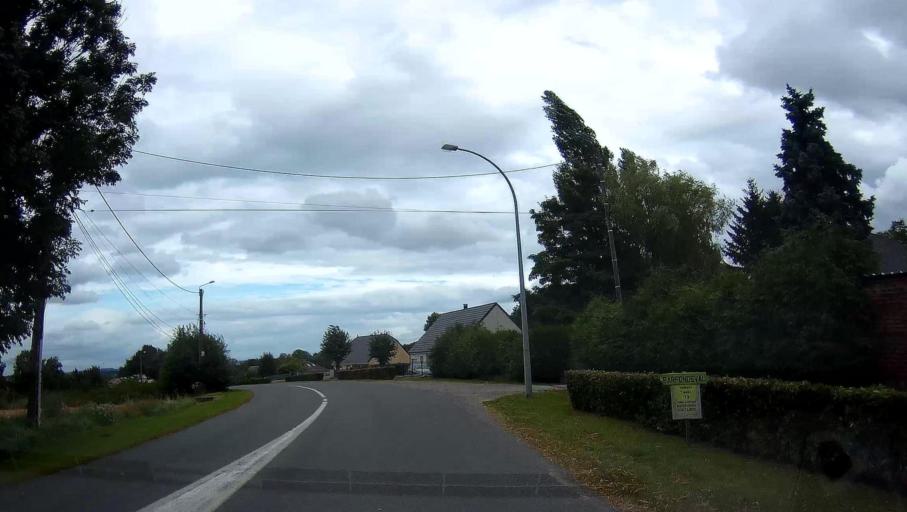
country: FR
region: Picardie
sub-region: Departement de l'Aisne
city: Rozoy-sur-Serre
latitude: 49.7045
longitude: 4.1132
